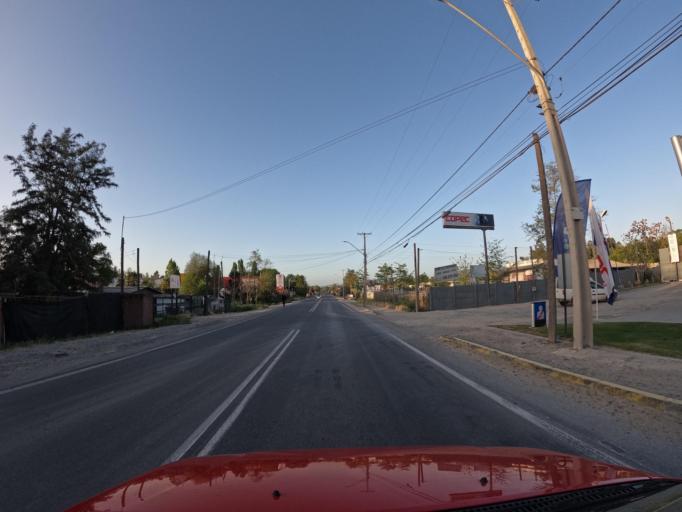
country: CL
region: O'Higgins
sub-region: Provincia de Cachapoal
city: San Vicente
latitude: -34.1744
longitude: -71.3977
